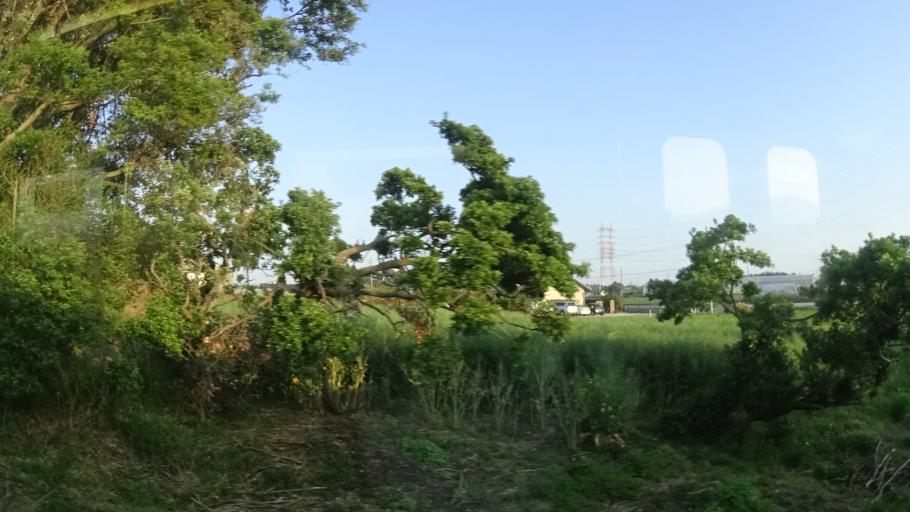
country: JP
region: Aichi
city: Tahara
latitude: 34.6693
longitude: 137.2983
